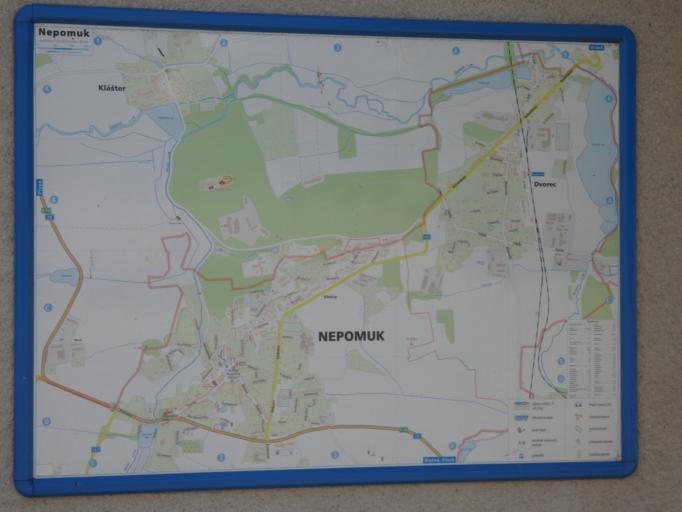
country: CZ
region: Plzensky
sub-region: Okres Plzen-Jih
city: Nepomuk
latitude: 49.4859
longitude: 13.5815
